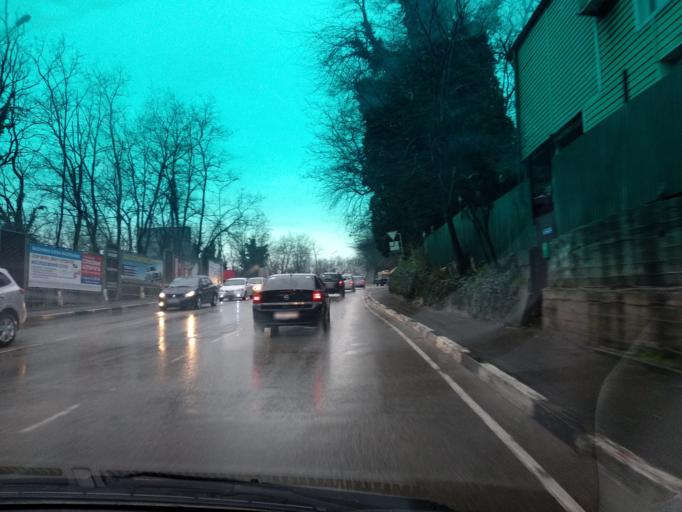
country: RU
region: Krasnodarskiy
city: Tuapse
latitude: 44.1046
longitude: 39.0862
